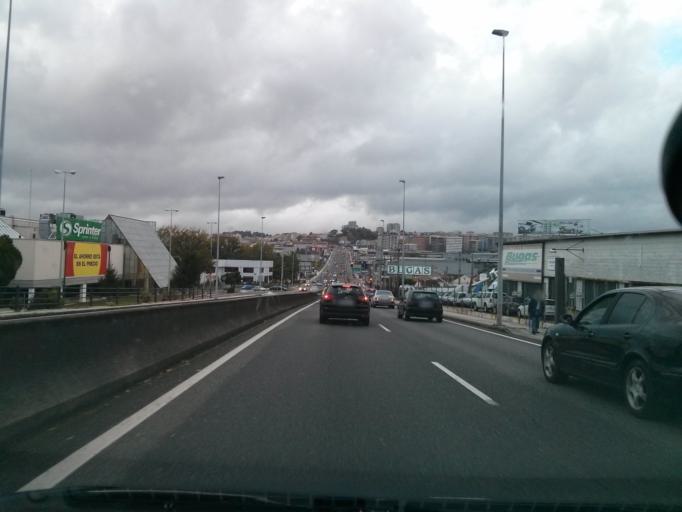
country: ES
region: Galicia
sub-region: Provincia de Pontevedra
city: Vigo
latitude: 42.2154
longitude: -8.6999
